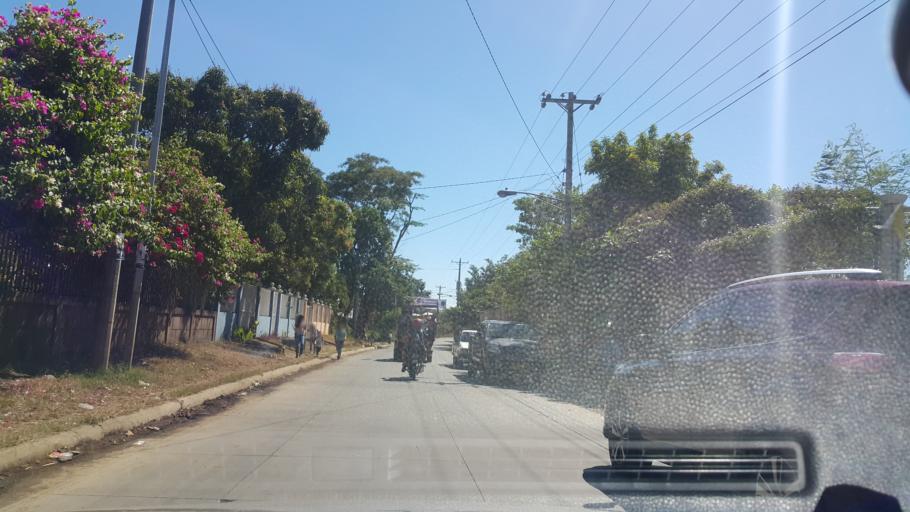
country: NI
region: Masaya
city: Ticuantepe
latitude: 12.0894
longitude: -86.1959
